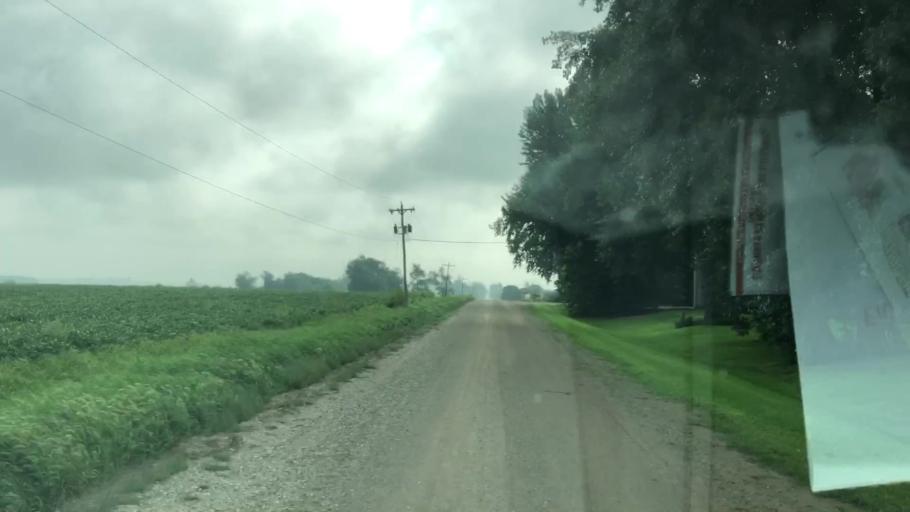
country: US
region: Iowa
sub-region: Sioux County
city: Hull
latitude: 43.2297
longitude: -96.0252
